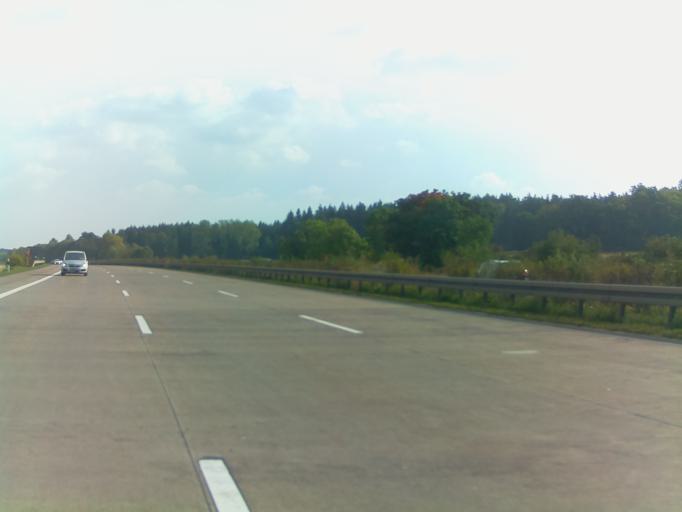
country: DE
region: Thuringia
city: Mechterstadt
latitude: 50.9273
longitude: 10.5117
